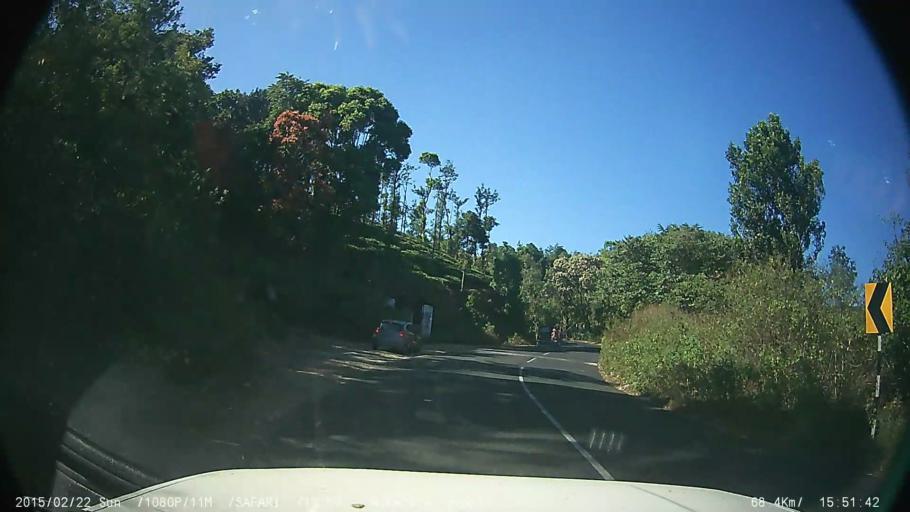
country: IN
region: Kerala
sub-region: Kottayam
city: Erattupetta
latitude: 9.5706
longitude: 77.0087
